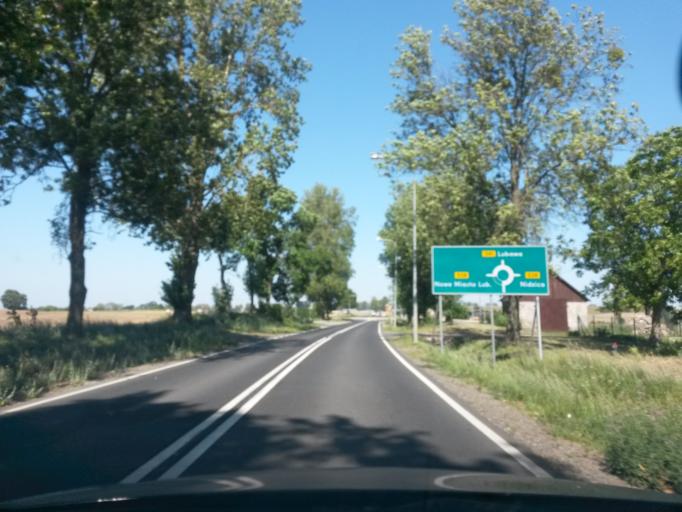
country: PL
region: Warmian-Masurian Voivodeship
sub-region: Powiat ilawski
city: Lubawa
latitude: 53.4063
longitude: 19.7974
